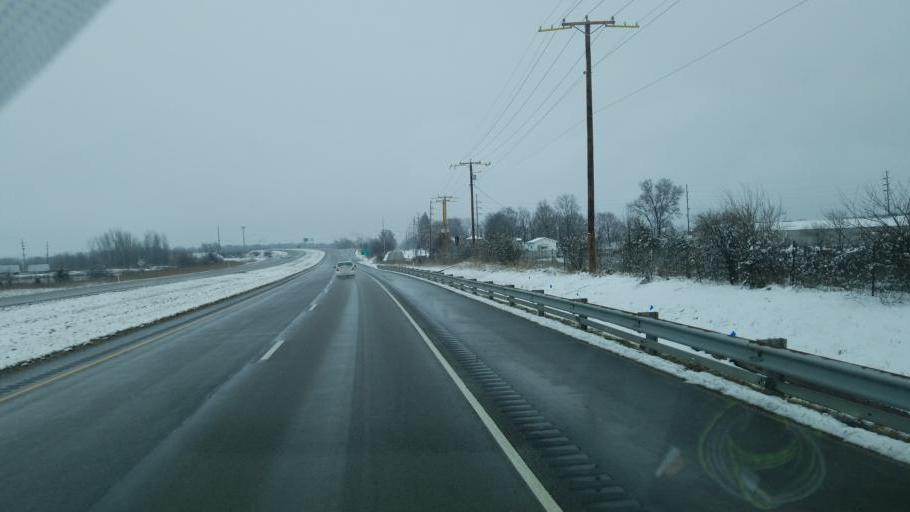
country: US
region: Indiana
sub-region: Delaware County
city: Muncie
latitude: 40.2514
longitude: -85.3680
